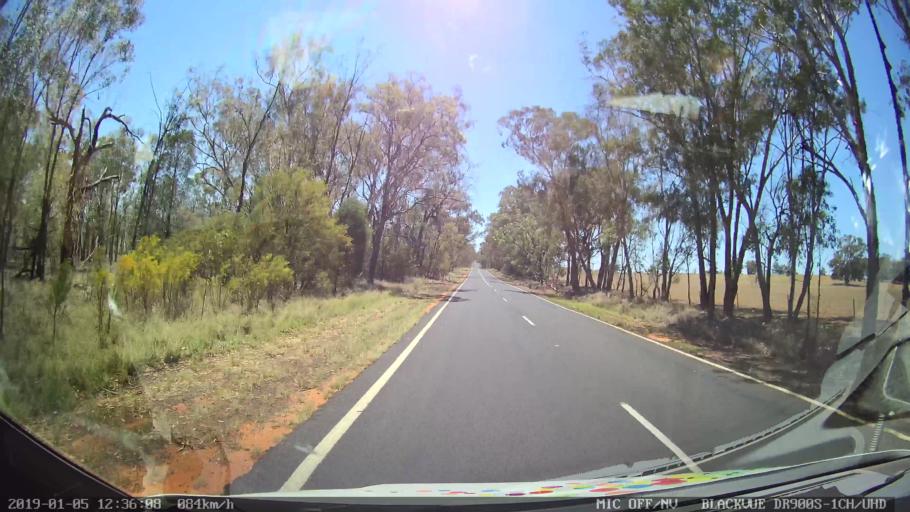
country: AU
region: New South Wales
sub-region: Warrumbungle Shire
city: Coonabarabran
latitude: -31.2079
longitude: 149.4359
